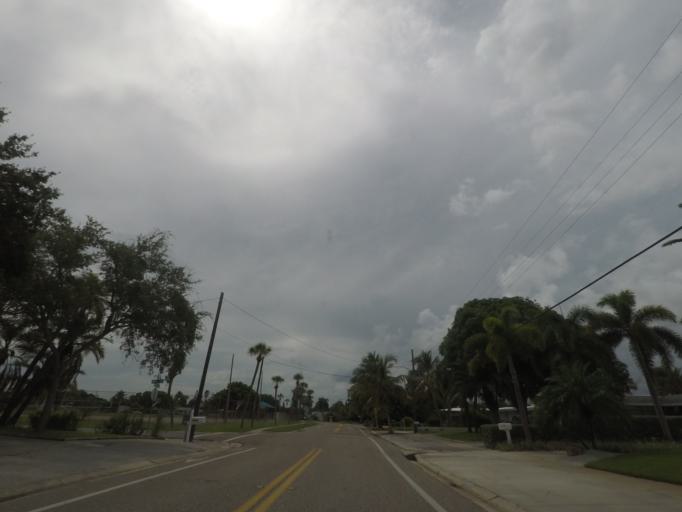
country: US
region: Florida
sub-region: Pinellas County
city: South Pasadena
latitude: 27.7480
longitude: -82.7573
